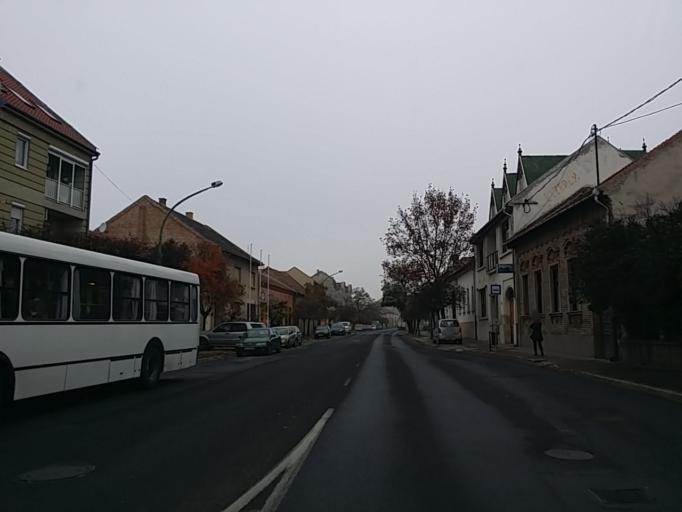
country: HU
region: Heves
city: Gyongyos
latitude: 47.7784
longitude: 19.9227
